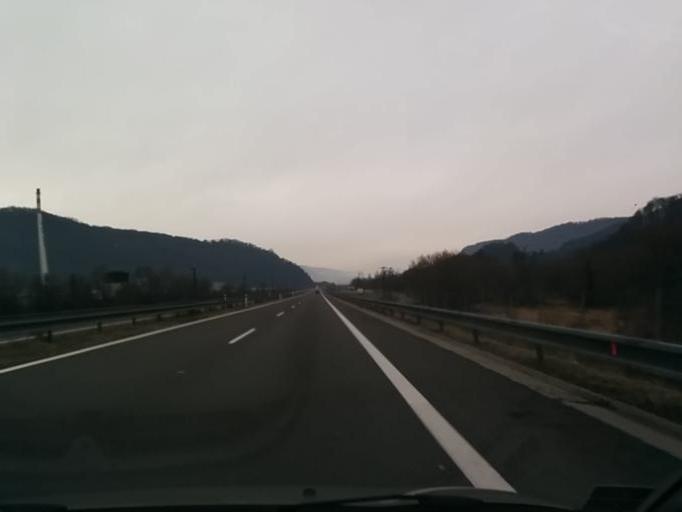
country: SK
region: Banskobystricky
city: Zarnovica
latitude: 48.4852
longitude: 18.7305
